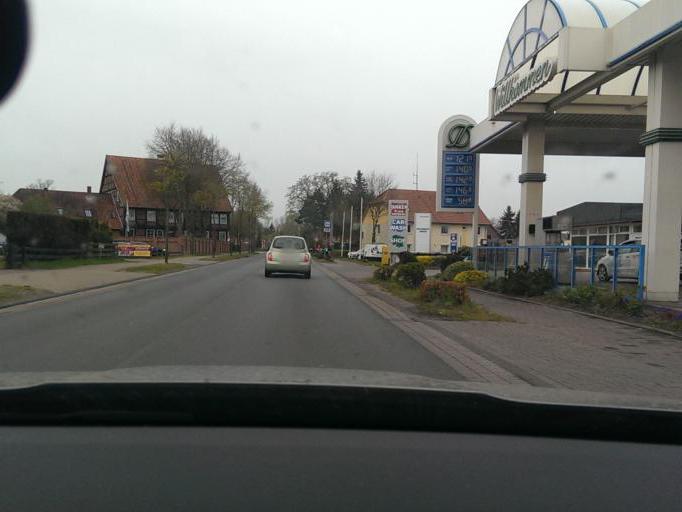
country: DE
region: Lower Saxony
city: Schwarmstedt
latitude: 52.6804
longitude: 9.6174
